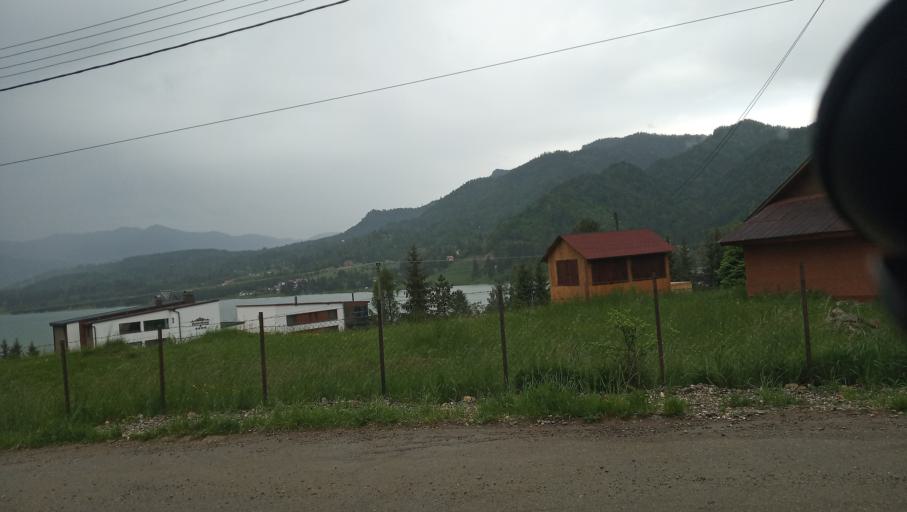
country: RO
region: Bistrita-Nasaud
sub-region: Comuna Tiha Bargaului
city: Tureac
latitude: 47.1710
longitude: 24.8858
